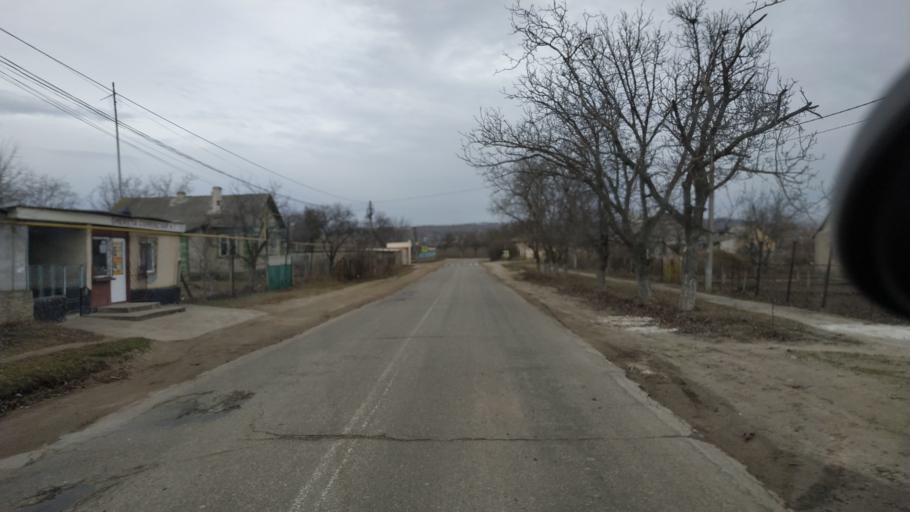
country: MD
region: Telenesti
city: Dubasari
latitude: 47.2468
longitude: 29.1389
